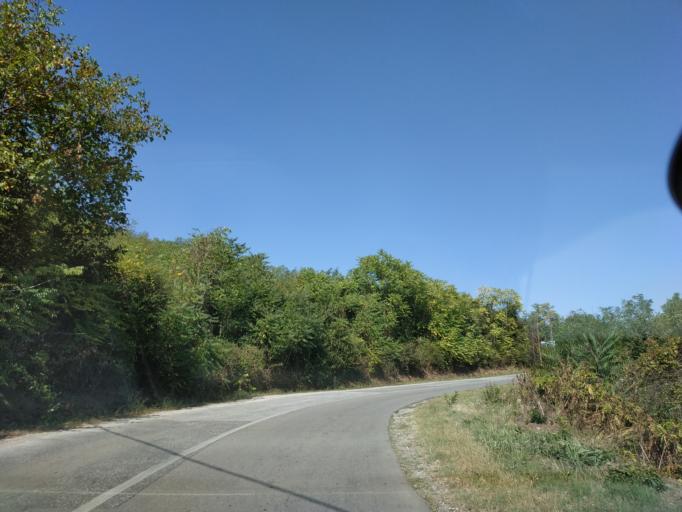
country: RS
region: Central Serbia
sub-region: Sumadijski Okrug
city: Topola
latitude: 44.2647
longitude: 20.6723
